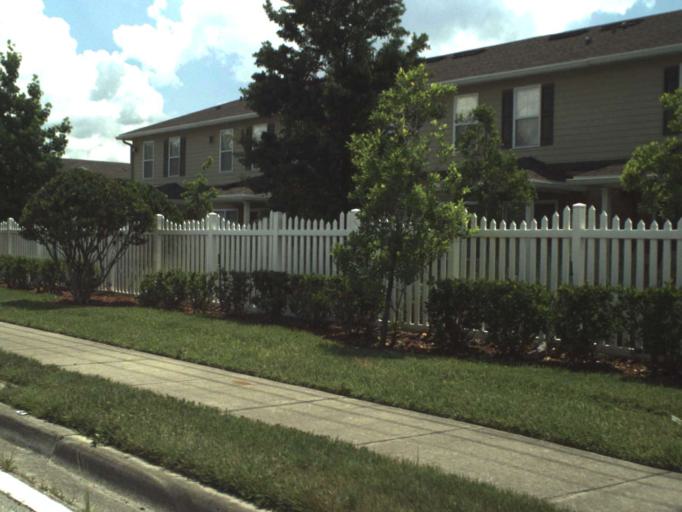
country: US
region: Florida
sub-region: Lake County
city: Leesburg
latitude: 28.8075
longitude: -81.9166
